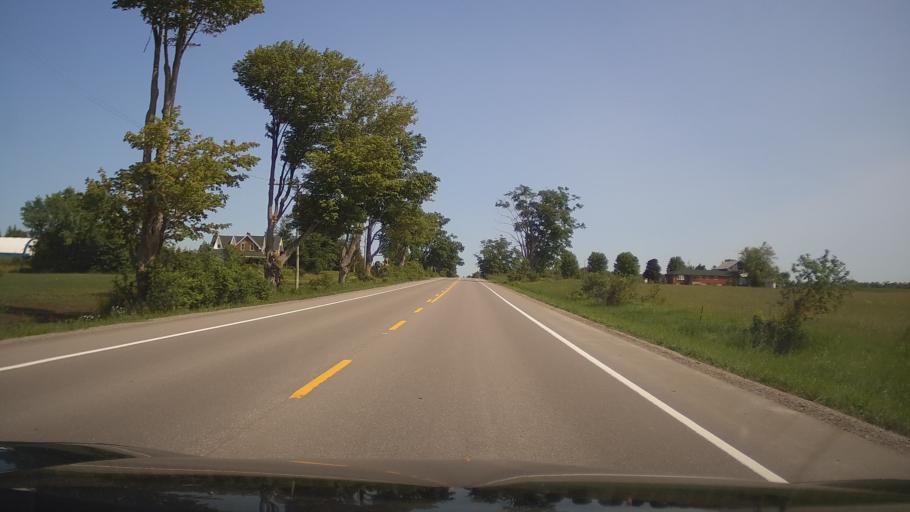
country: CA
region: Ontario
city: Omemee
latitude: 44.3471
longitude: -78.8861
